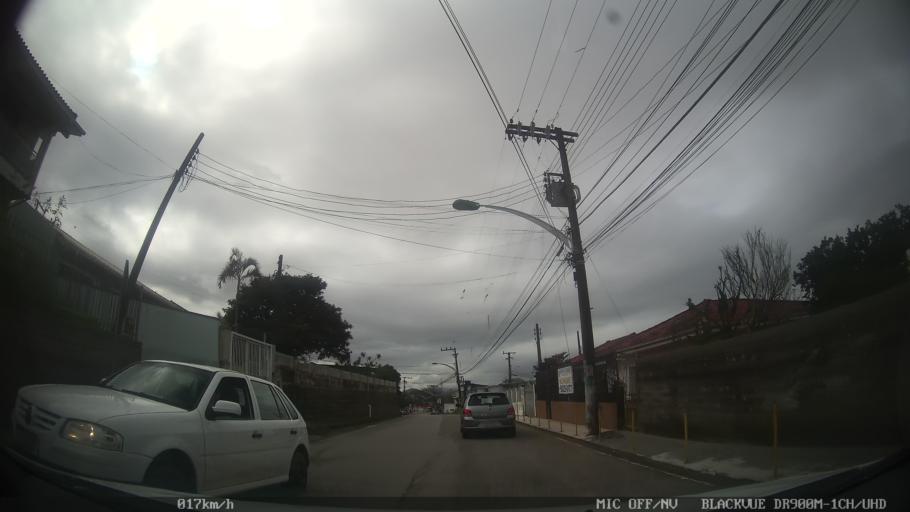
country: BR
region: Santa Catarina
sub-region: Biguacu
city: Biguacu
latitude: -27.5340
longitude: -48.6433
